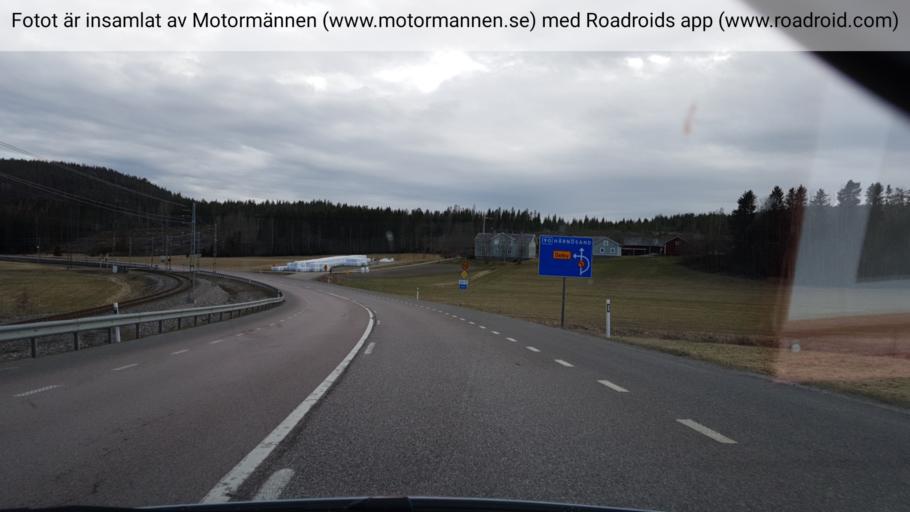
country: SE
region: Vaesternorrland
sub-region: Kramfors Kommun
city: Kramfors
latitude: 62.8269
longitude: 17.8484
